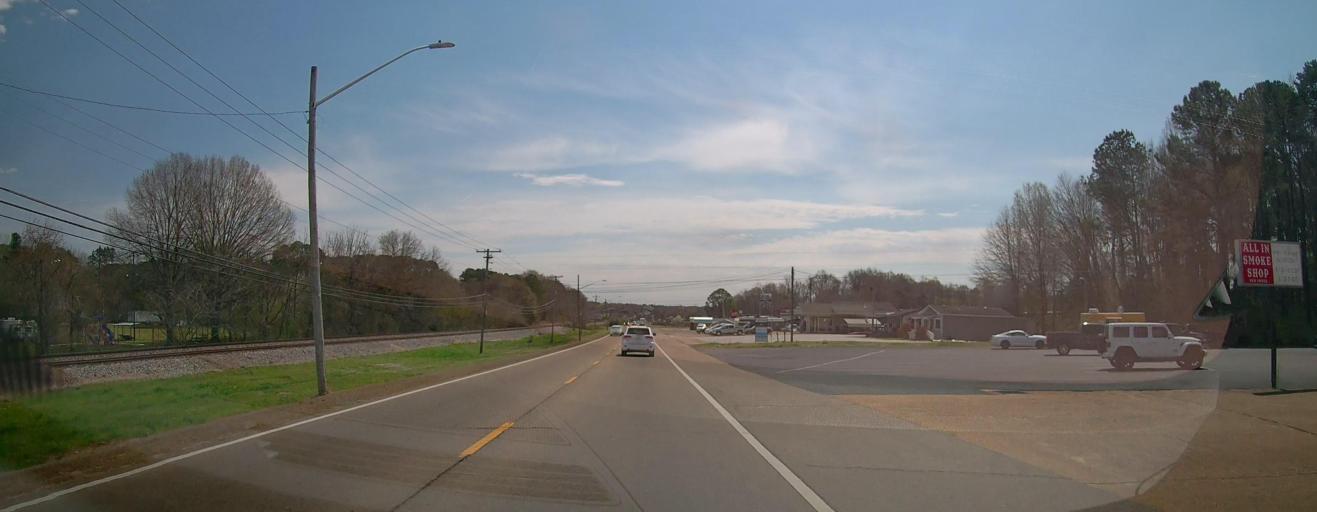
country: US
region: Mississippi
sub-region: Union County
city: New Albany
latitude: 34.5027
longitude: -89.0273
